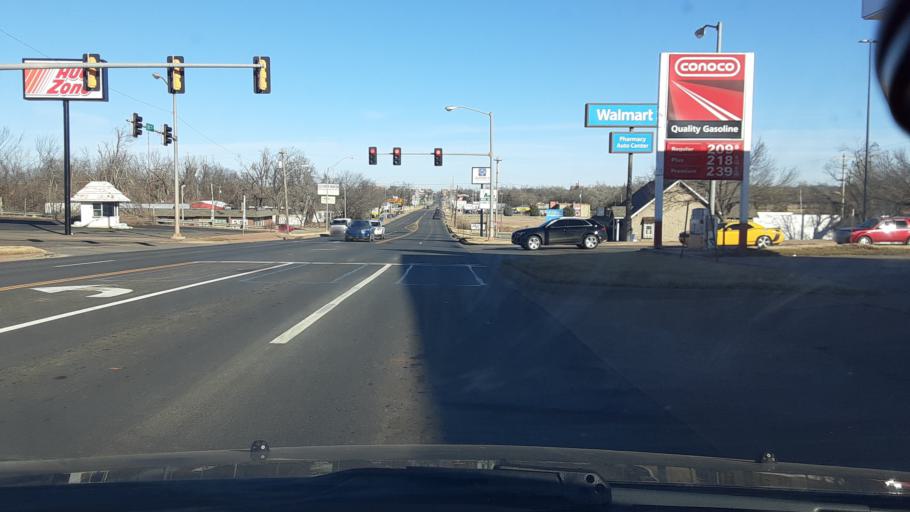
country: US
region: Oklahoma
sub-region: Logan County
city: Guthrie
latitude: 35.8622
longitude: -97.4253
